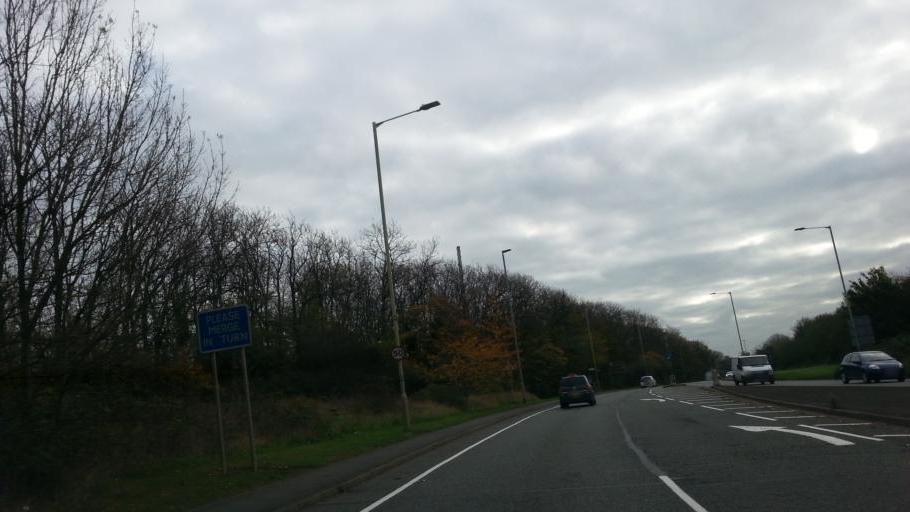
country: GB
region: England
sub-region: Leicestershire
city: Anstey
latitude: 52.6646
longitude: -1.1769
